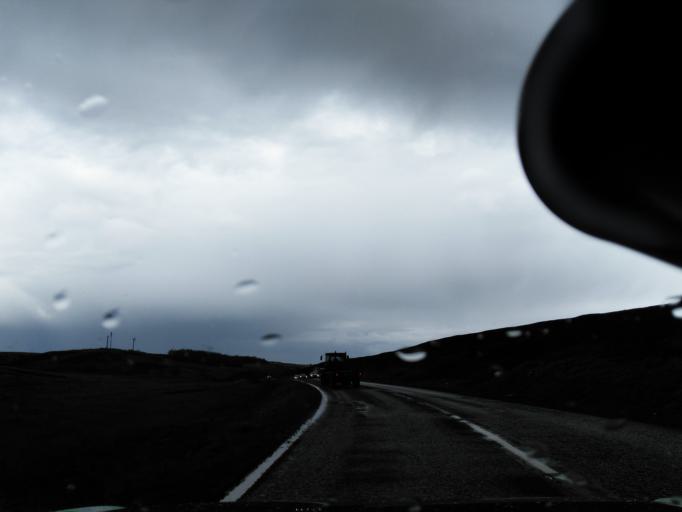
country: GB
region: England
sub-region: Bradford
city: Ilkley
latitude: 53.9907
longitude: -1.7987
